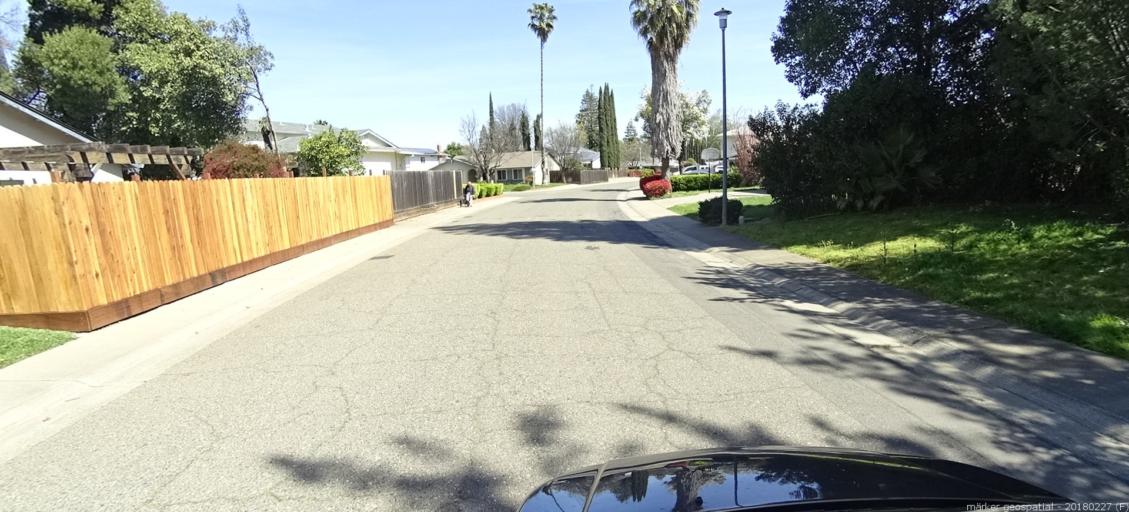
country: US
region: California
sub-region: Sacramento County
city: La Riviera
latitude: 38.5599
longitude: -121.3513
